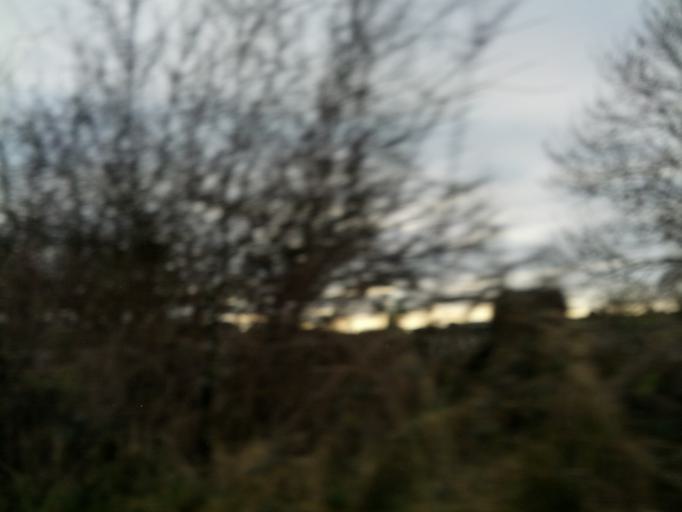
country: IE
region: Connaught
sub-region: County Galway
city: Oranmore
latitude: 53.2113
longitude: -8.8520
